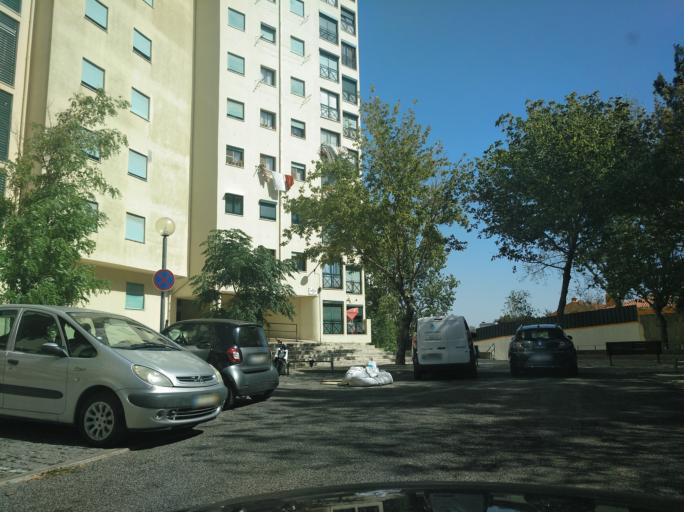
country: PT
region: Lisbon
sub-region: Lisbon
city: Lisbon
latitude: 38.7436
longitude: -9.1195
